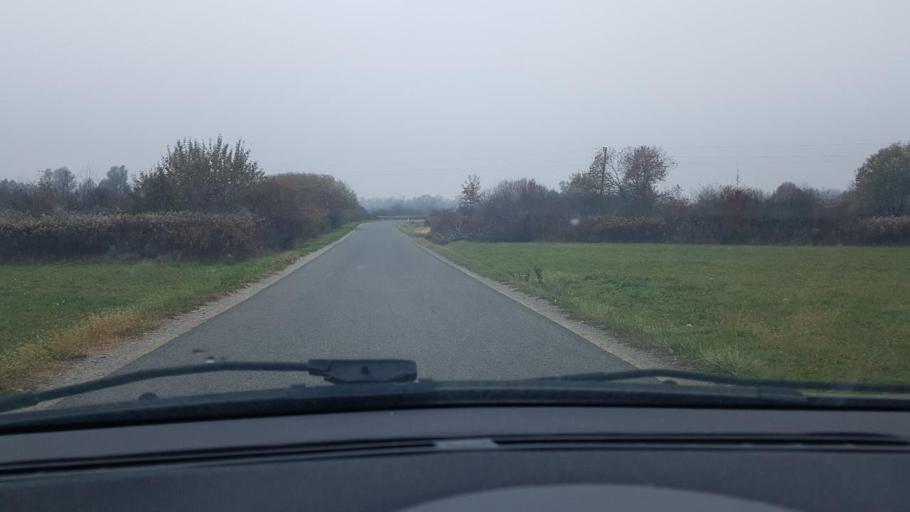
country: HR
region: Krapinsko-Zagorska
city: Marija Bistrica
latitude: 46.0707
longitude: 16.1813
